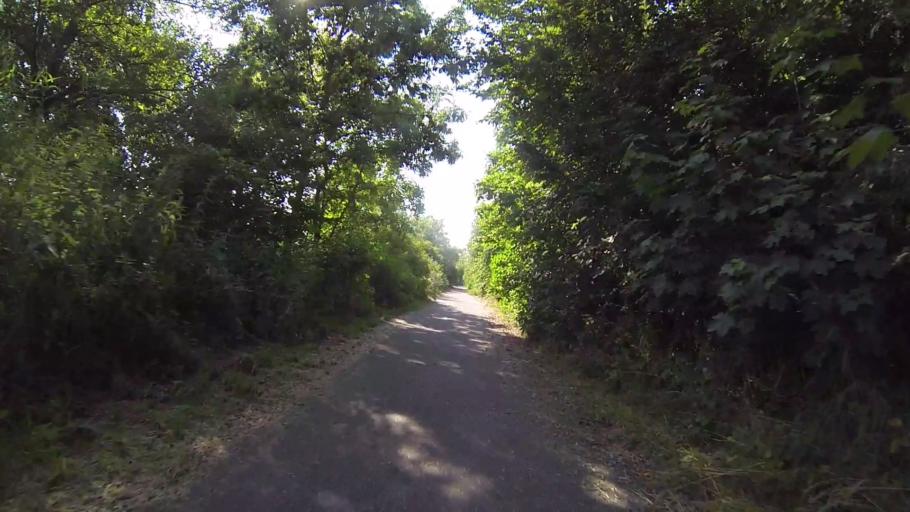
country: DE
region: Baden-Wuerttemberg
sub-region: Tuebingen Region
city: Erbach
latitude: 48.3495
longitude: 9.9311
